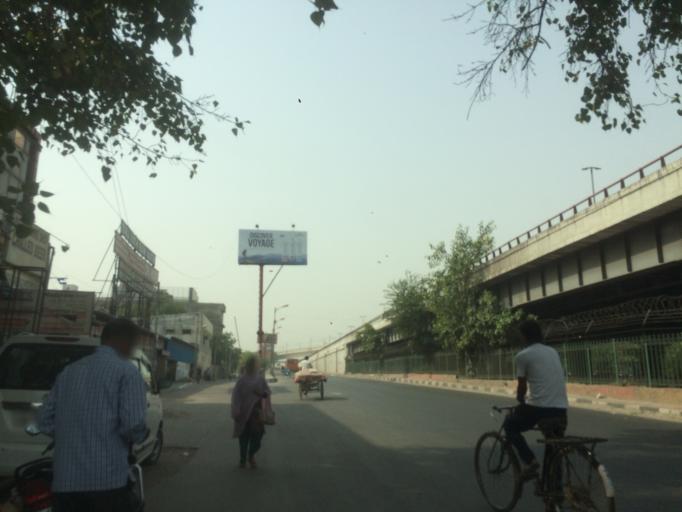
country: IN
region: NCT
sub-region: West Delhi
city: Nangloi Jat
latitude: 28.6142
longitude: 77.1079
